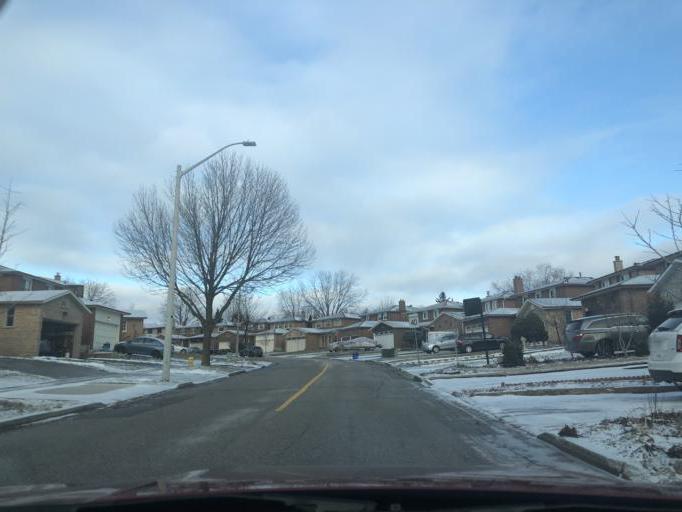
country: CA
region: Ontario
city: Markham
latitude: 43.8715
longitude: -79.2415
